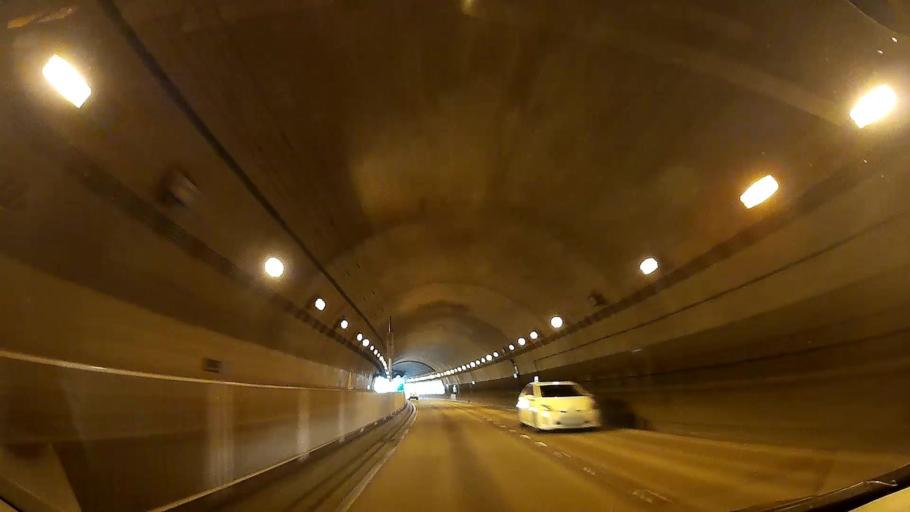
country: JP
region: Tokyo
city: Hachioji
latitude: 35.6764
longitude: 139.3409
